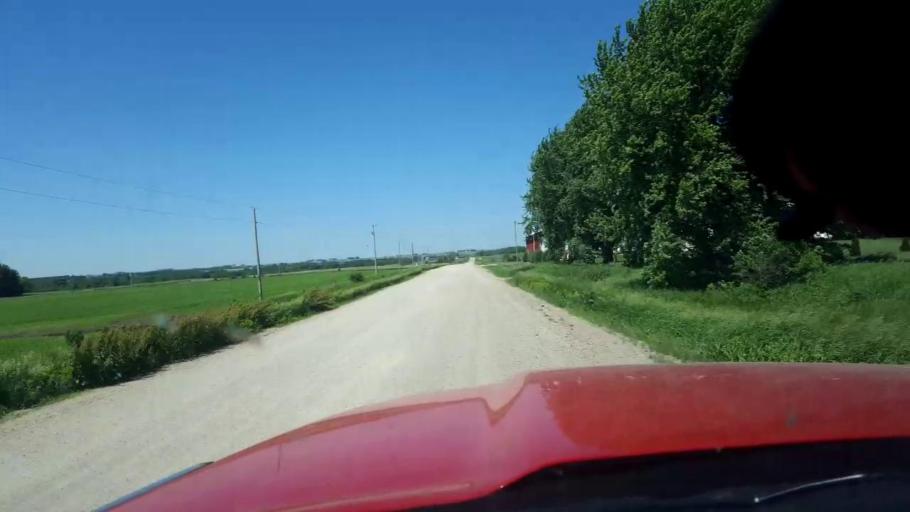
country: US
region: Iowa
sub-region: Chickasaw County
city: New Hampton
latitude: 43.2135
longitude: -92.2554
